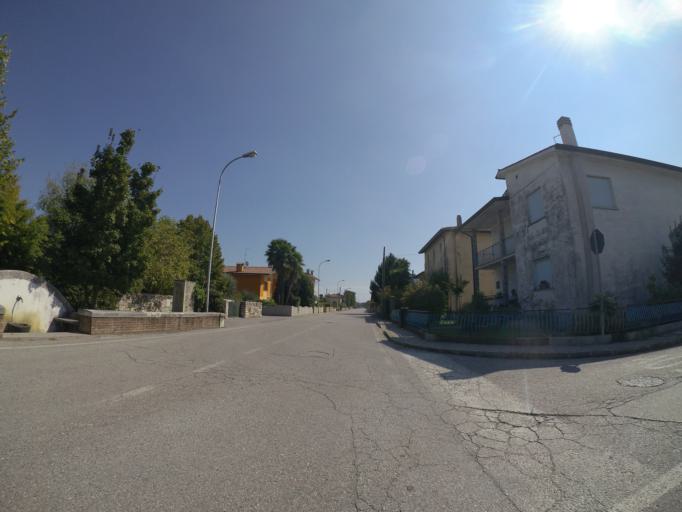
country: IT
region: Friuli Venezia Giulia
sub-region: Provincia di Udine
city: Muzzana del Turgnano
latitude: 45.8146
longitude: 13.1263
